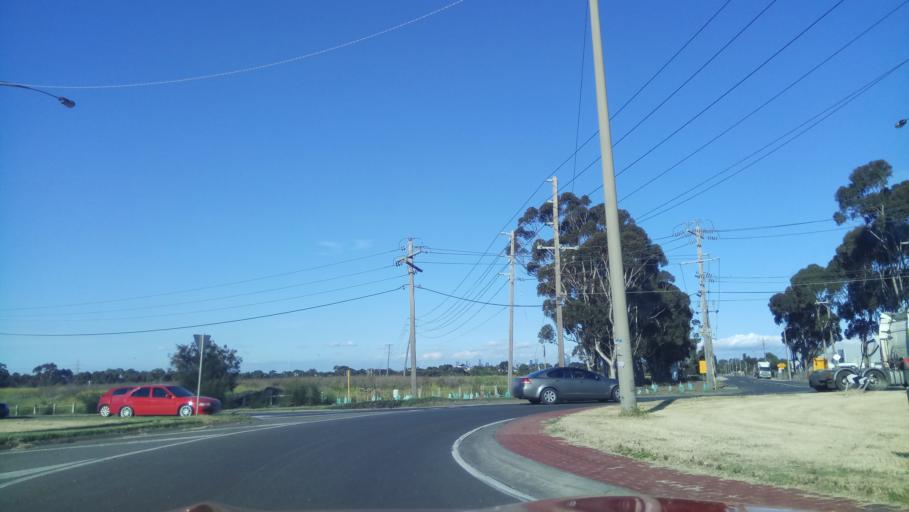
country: AU
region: Victoria
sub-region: Hobsons Bay
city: Altona North
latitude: -37.8314
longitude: 144.8265
